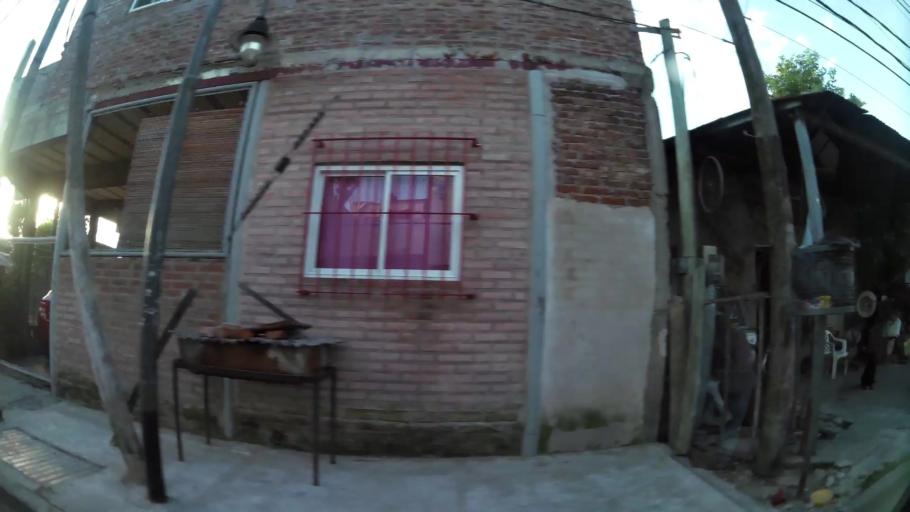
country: AR
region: Buenos Aires
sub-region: Partido de Tigre
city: Tigre
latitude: -34.4471
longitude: -58.5709
